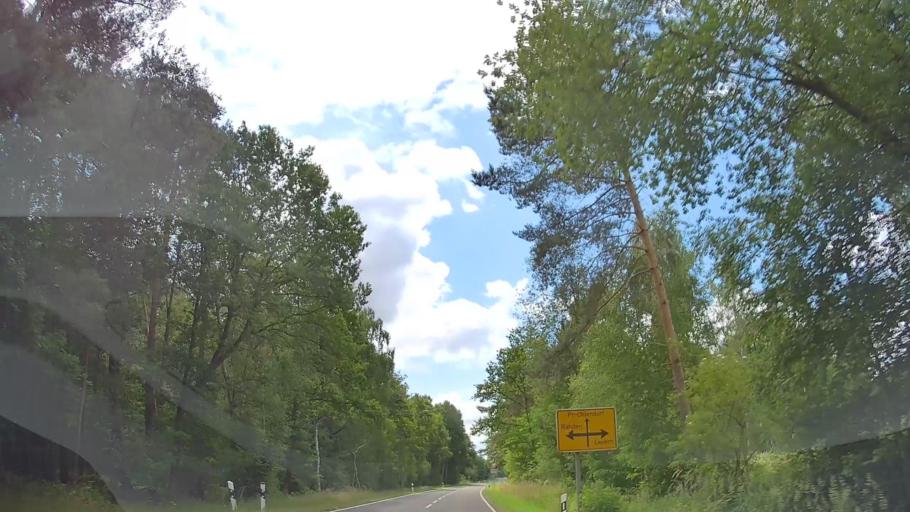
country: DE
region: North Rhine-Westphalia
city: Rahden
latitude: 52.4191
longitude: 8.5195
